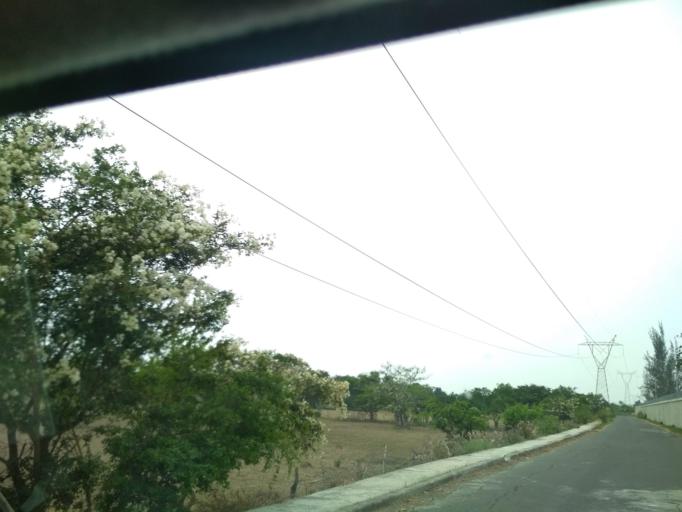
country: MX
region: Veracruz
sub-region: Medellin
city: Fraccionamiento Arboledas San Ramon
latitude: 19.0880
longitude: -96.1479
